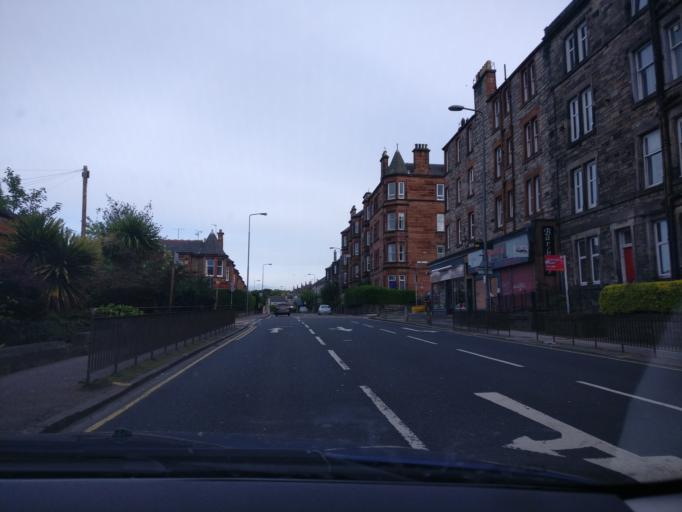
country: GB
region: Scotland
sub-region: West Lothian
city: Seafield
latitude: 55.9547
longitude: -3.1488
